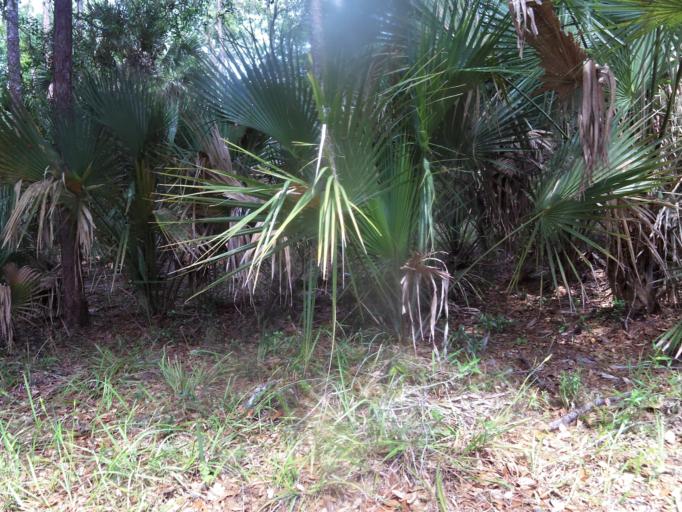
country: US
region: Florida
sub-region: Flagler County
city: Flagler Beach
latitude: 29.4007
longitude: -81.1215
